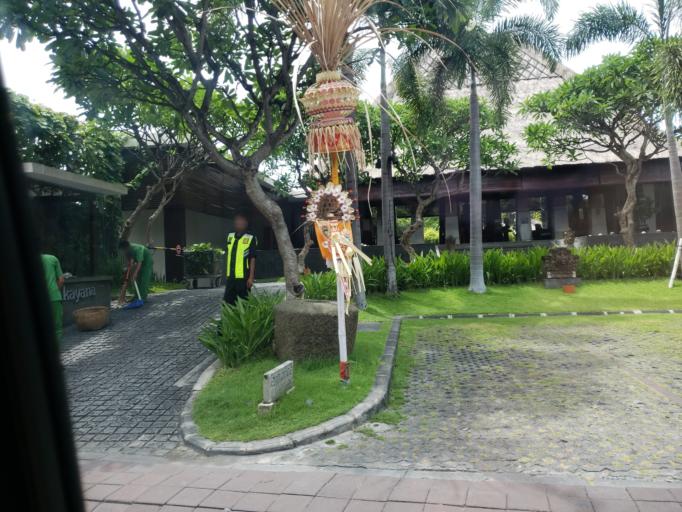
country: ID
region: Bali
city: Kuta
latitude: -8.6777
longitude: 115.1539
